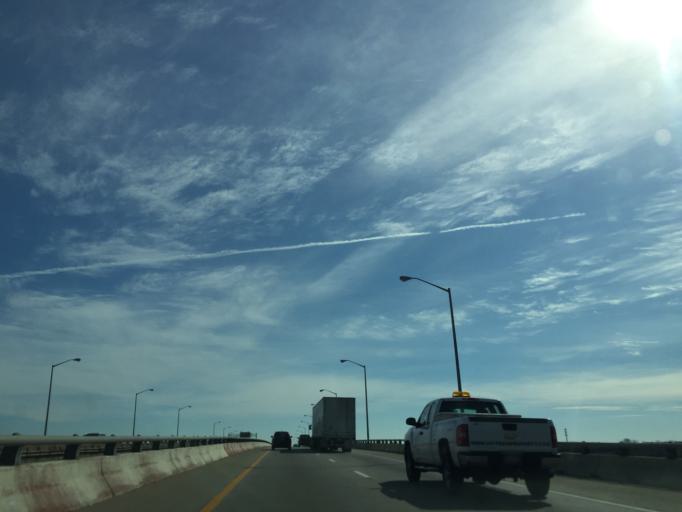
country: US
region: Virginia
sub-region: City of Hampton
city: East Hampton
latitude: 36.9632
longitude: -76.2758
